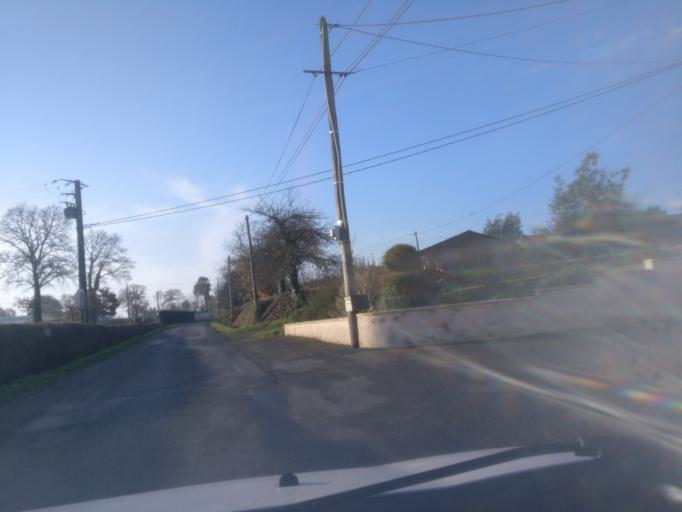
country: FR
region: Brittany
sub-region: Departement d'Ille-et-Vilaine
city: Saint-Jean-sur-Couesnon
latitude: 48.2742
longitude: -1.3659
